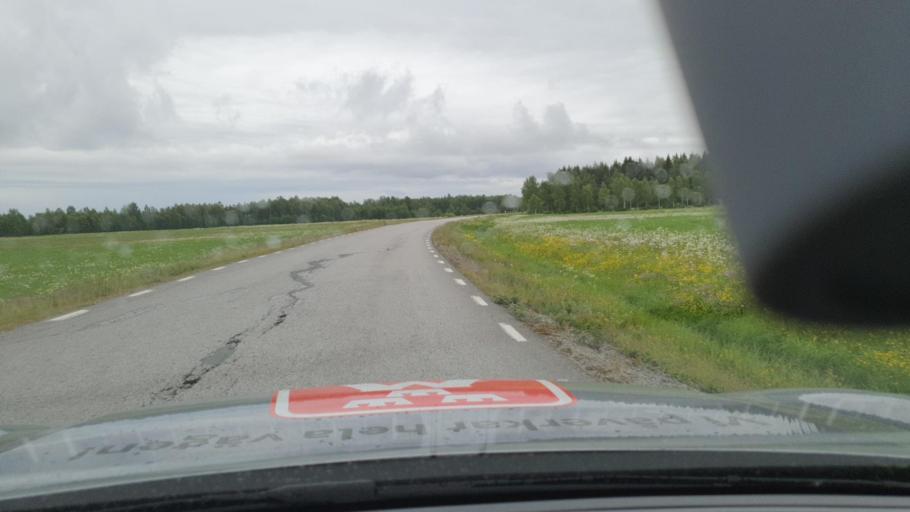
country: SE
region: Norrbotten
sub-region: Kalix Kommun
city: Toere
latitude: 65.8826
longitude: 22.6631
